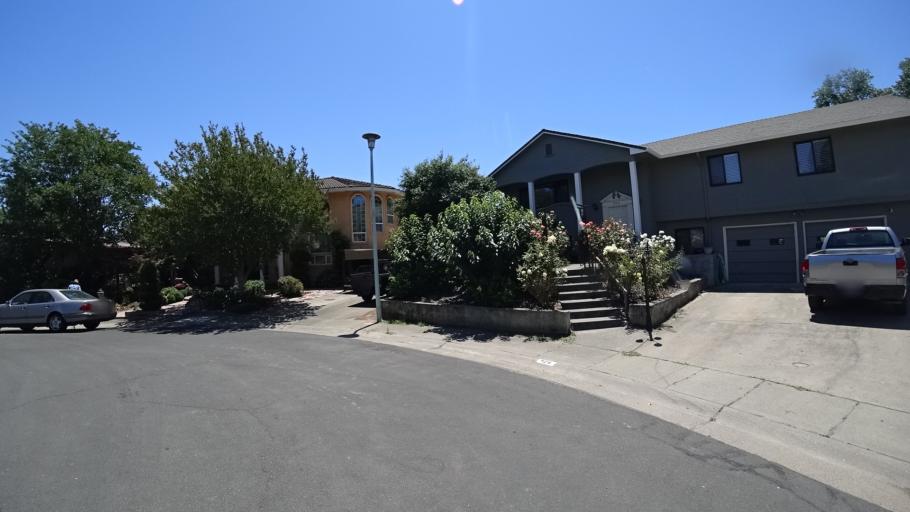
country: US
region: California
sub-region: Yolo County
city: West Sacramento
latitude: 38.5251
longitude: -121.5251
